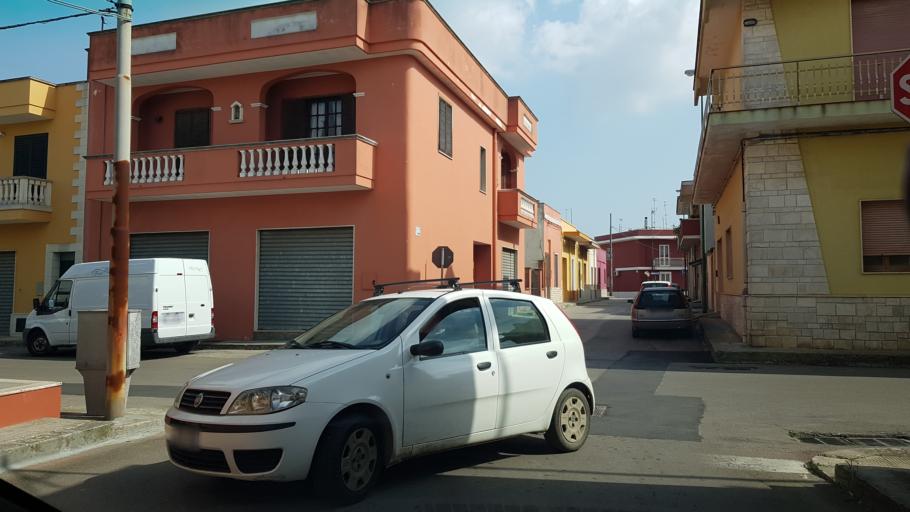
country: IT
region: Apulia
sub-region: Provincia di Brindisi
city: Torchiarolo
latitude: 40.4877
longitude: 18.0520
